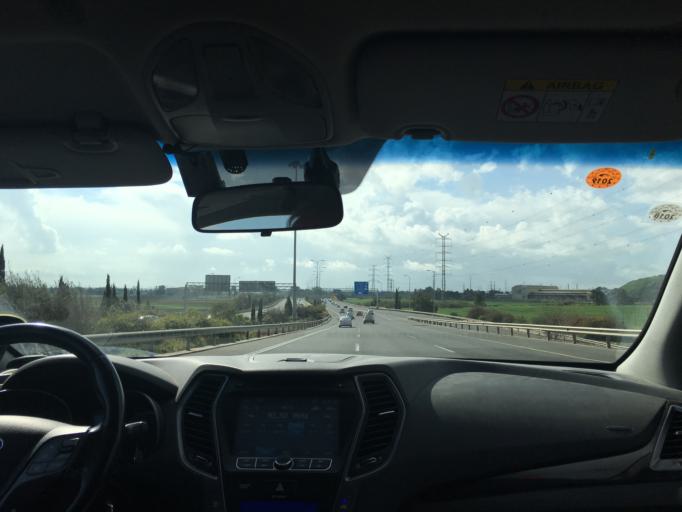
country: IL
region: Tel Aviv
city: Azor
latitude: 32.0364
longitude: 34.8295
